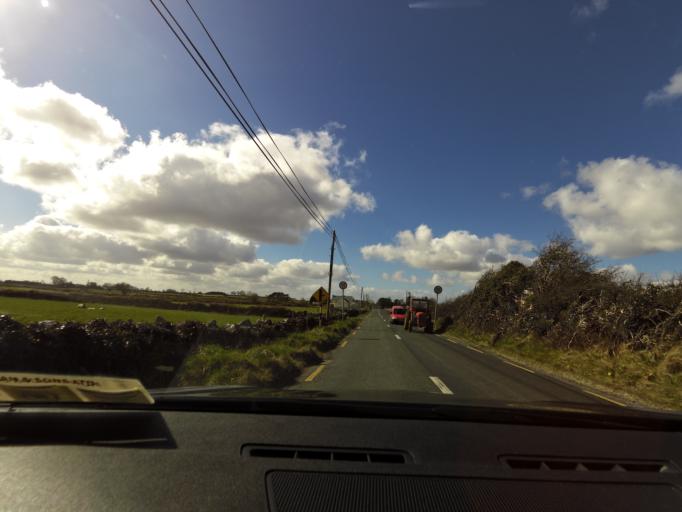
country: IE
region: Connaught
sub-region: County Galway
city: Athenry
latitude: 53.4216
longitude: -8.5605
